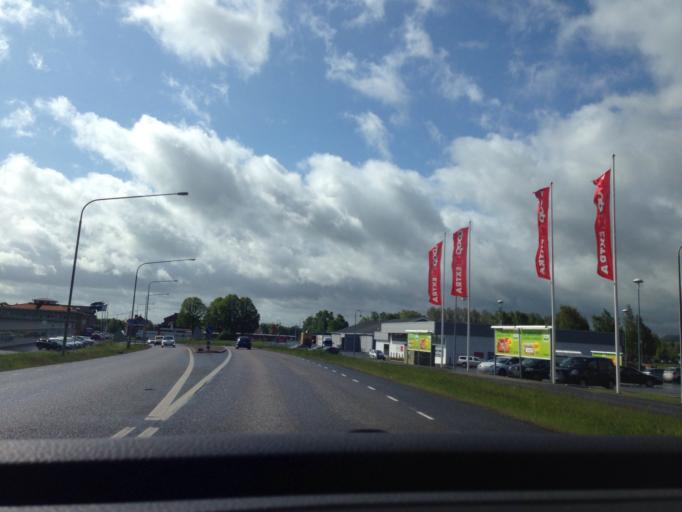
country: SE
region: Vaestra Goetaland
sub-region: Skovde Kommun
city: Skoevde
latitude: 58.3875
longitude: 13.8330
